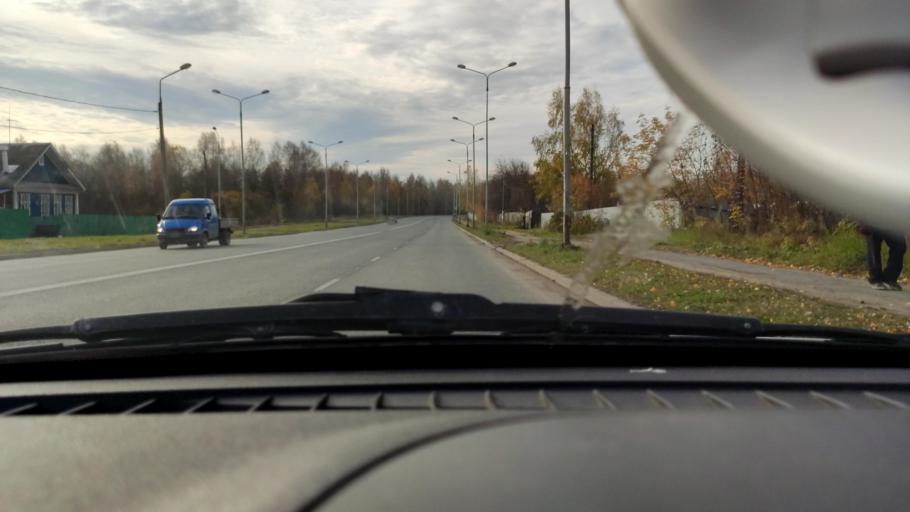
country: RU
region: Perm
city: Polazna
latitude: 58.1138
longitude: 56.4002
